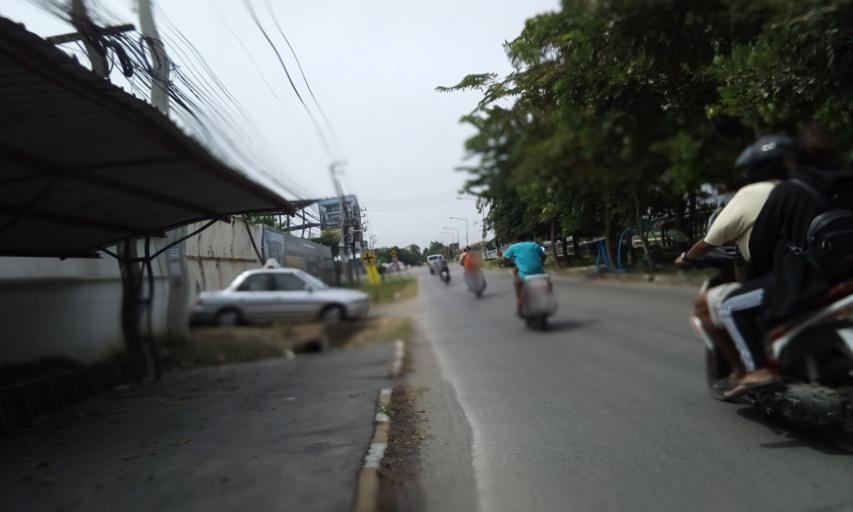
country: TH
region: Pathum Thani
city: Ban Rangsit
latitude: 14.0311
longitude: 100.7634
